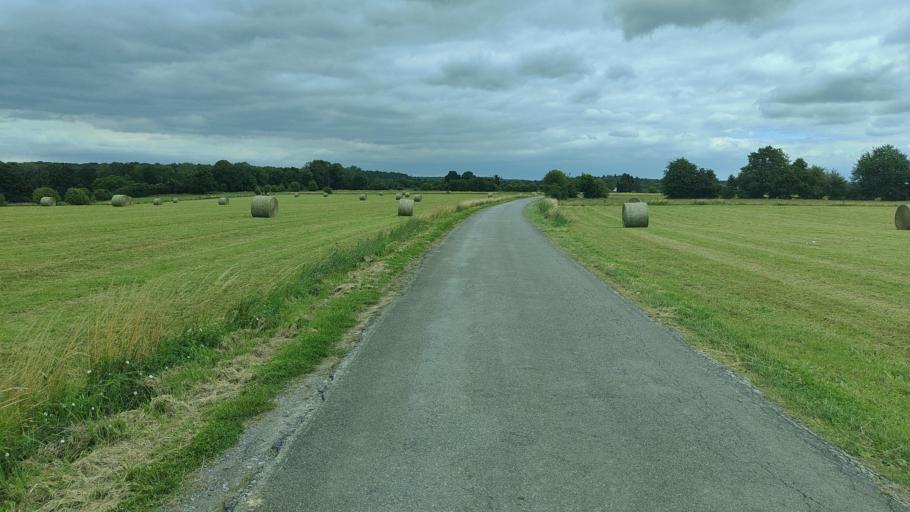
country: BE
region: Wallonia
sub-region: Province du Hainaut
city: Chimay
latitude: 50.0578
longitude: 4.3540
